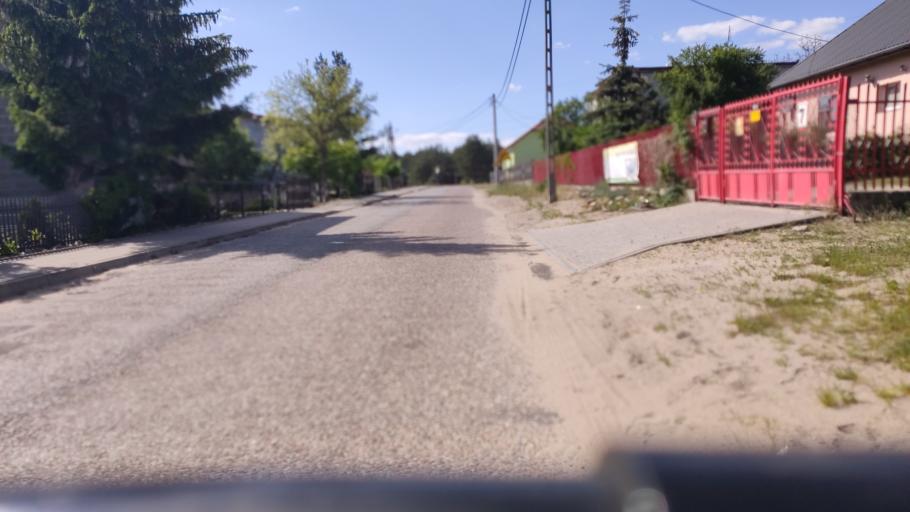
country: PL
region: Kujawsko-Pomorskie
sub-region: Wloclawek
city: Wloclawek
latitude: 52.5931
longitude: 19.0882
